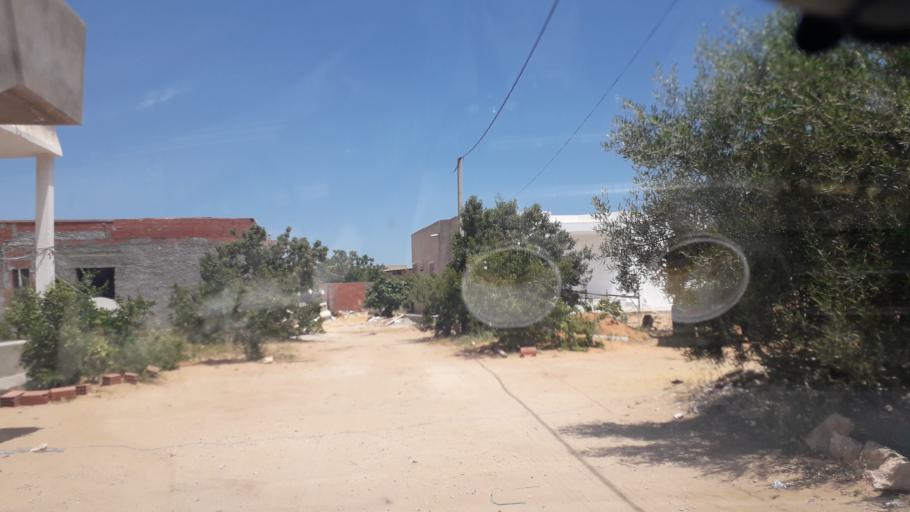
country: TN
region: Safaqis
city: Al Qarmadah
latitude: 34.8159
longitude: 10.7693
